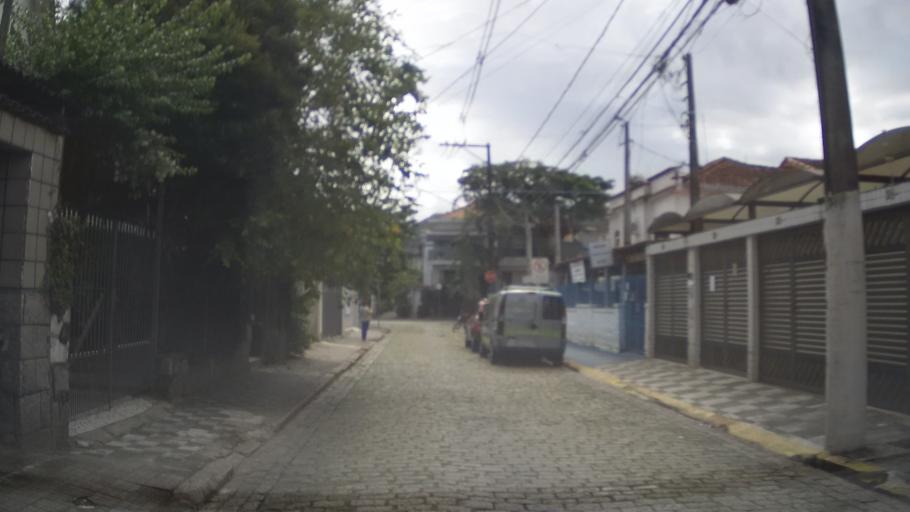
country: BR
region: Sao Paulo
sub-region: Santos
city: Santos
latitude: -23.9521
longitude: -46.3328
